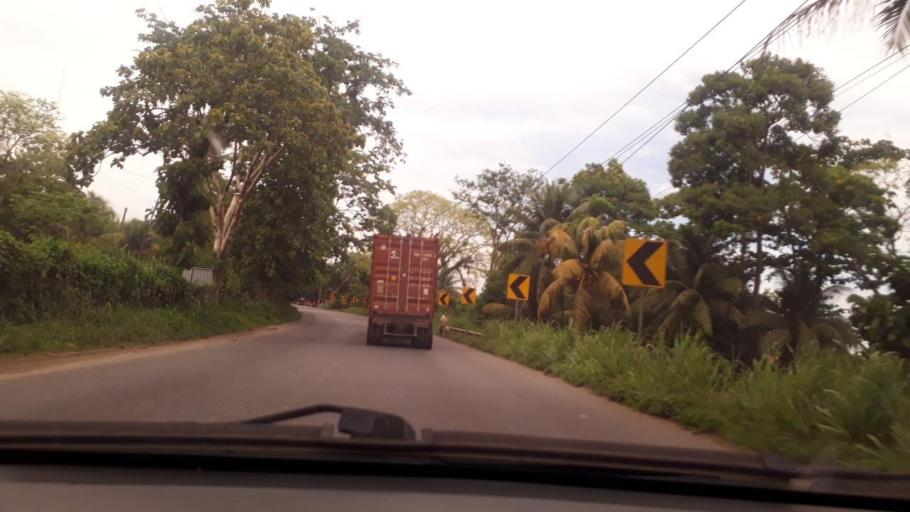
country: GT
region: Izabal
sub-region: Municipio de Puerto Barrios
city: Puerto Barrios
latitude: 15.5921
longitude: -88.5742
